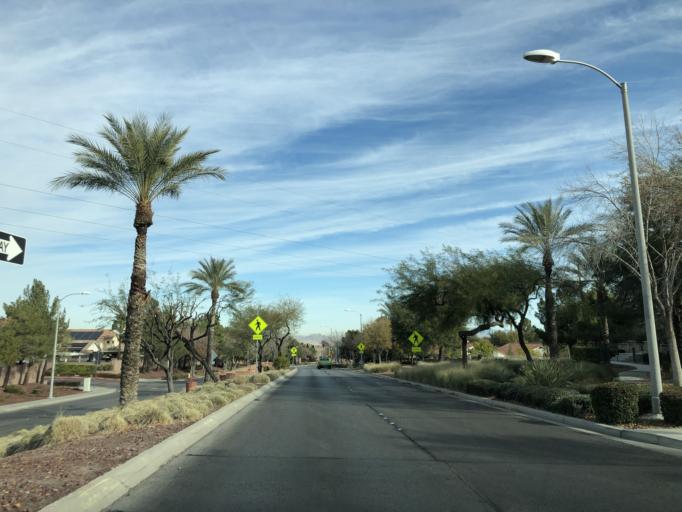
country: US
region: Nevada
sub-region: Clark County
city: Whitney
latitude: 36.0206
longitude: -115.0684
